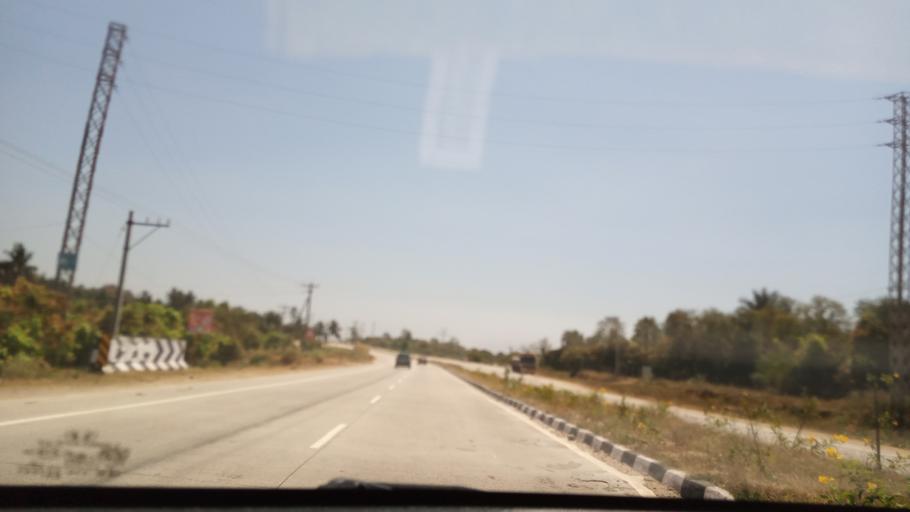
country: IN
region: Andhra Pradesh
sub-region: Chittoor
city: Chittoor
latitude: 13.1990
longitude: 78.9732
